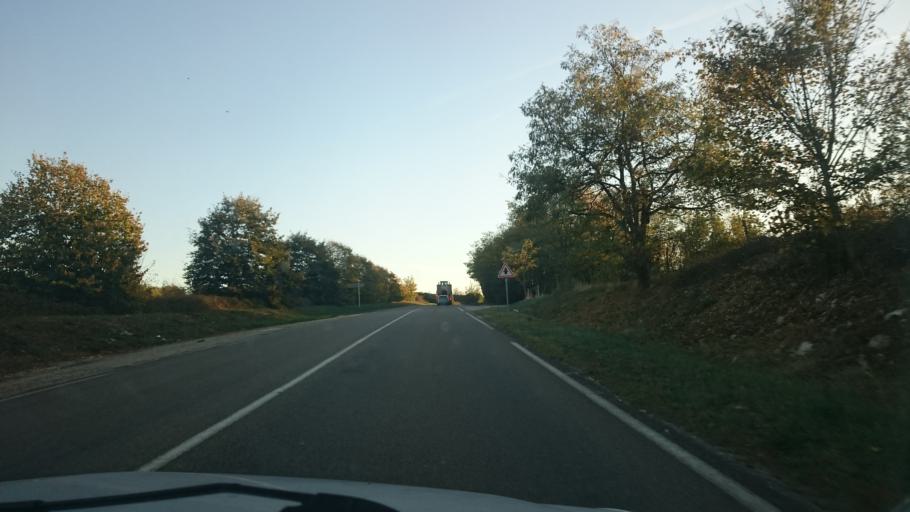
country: FR
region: Franche-Comte
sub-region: Departement du Doubs
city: Quingey
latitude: 47.0846
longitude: 5.8831
